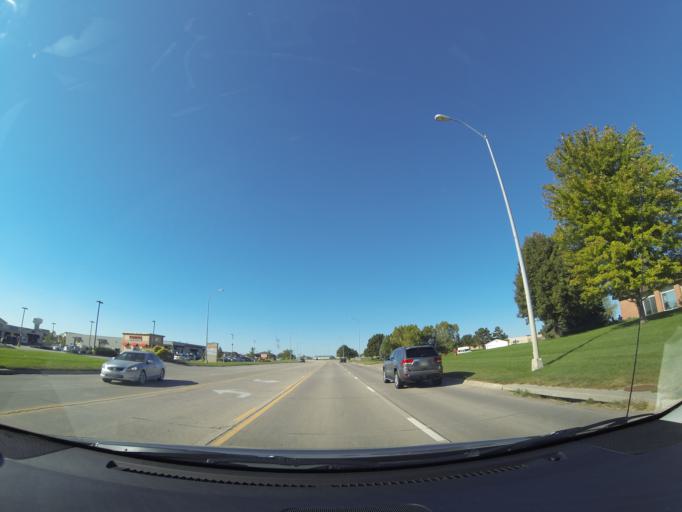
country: US
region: Nebraska
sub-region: Sarpy County
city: Gretna
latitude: 41.1337
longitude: -96.2481
